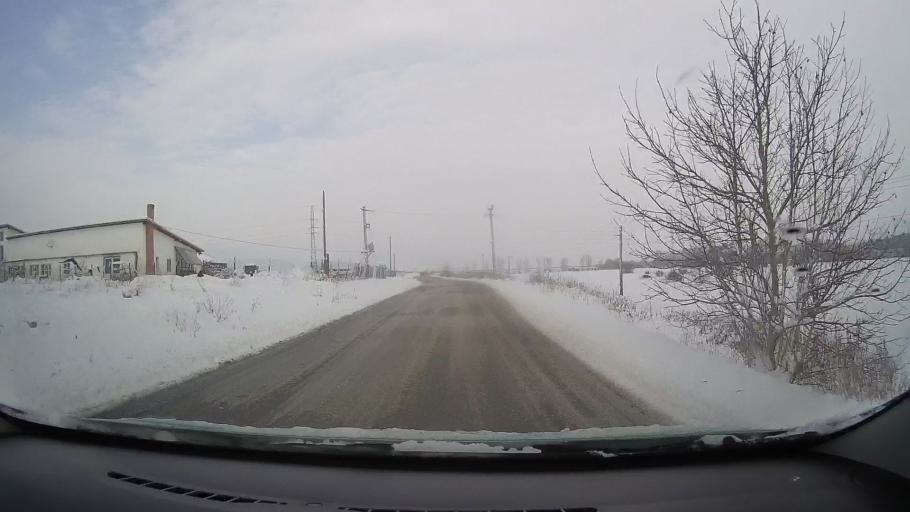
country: RO
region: Alba
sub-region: Comuna Pianu
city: Pianu de Jos
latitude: 45.9528
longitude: 23.4781
